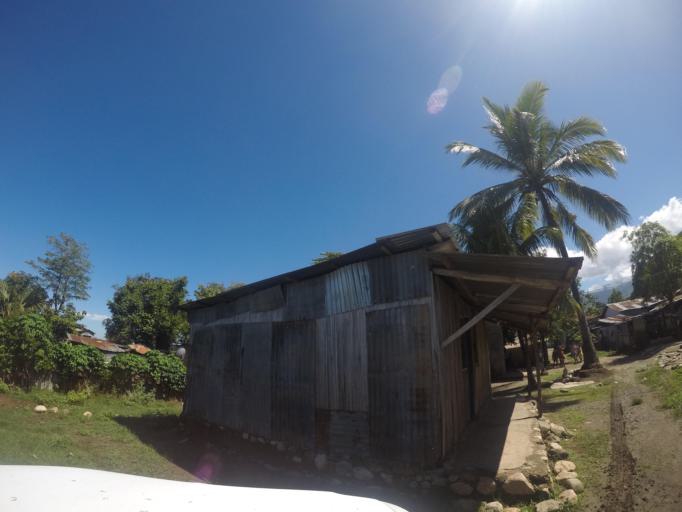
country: TL
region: Bobonaro
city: Maliana
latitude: -8.9844
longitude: 125.2099
